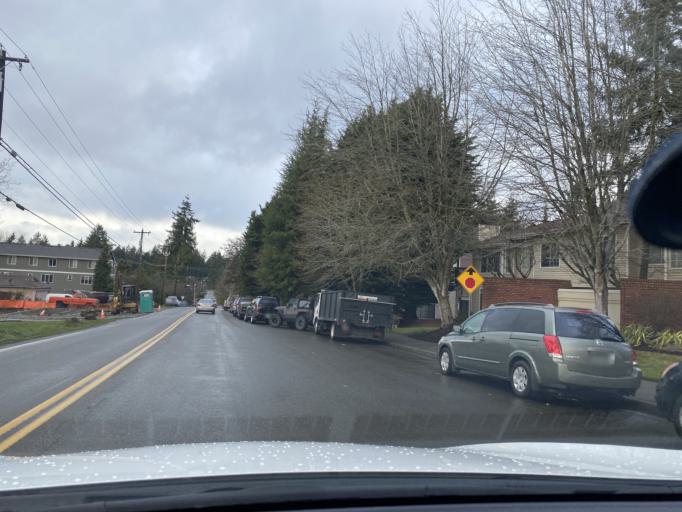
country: US
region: Washington
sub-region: Snohomish County
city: Alderwood Manor
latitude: 47.8502
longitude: -122.2960
